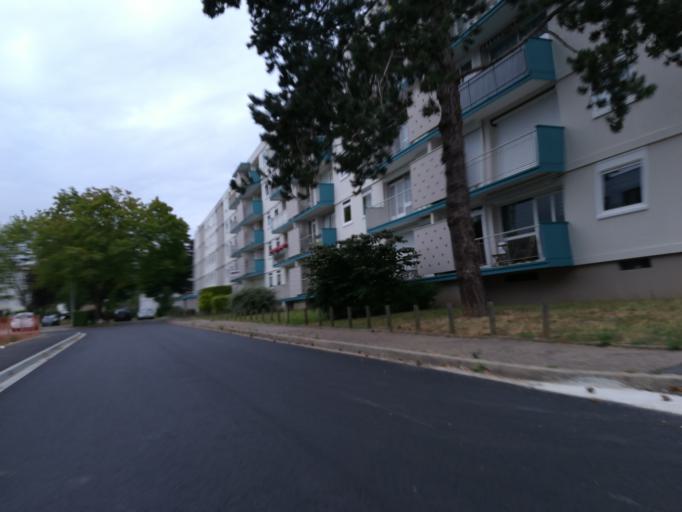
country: FR
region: Haute-Normandie
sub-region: Departement de la Seine-Maritime
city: Deville-les-Rouen
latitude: 49.4631
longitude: 1.0720
